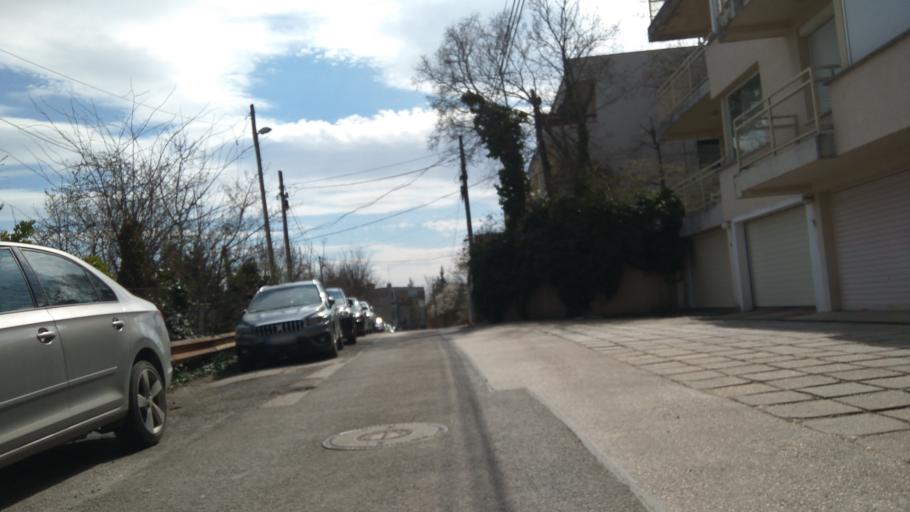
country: HU
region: Budapest
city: Budapest XII. keruelet
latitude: 47.4978
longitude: 19.0052
